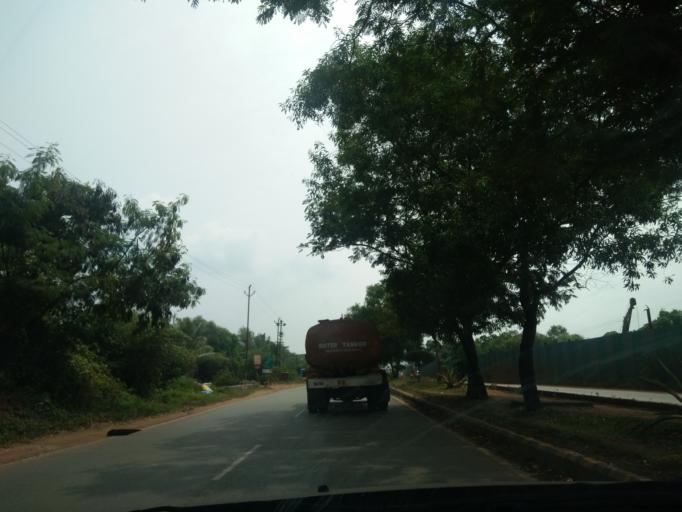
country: IN
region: Goa
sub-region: North Goa
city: Panaji
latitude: 15.4927
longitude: 73.8420
